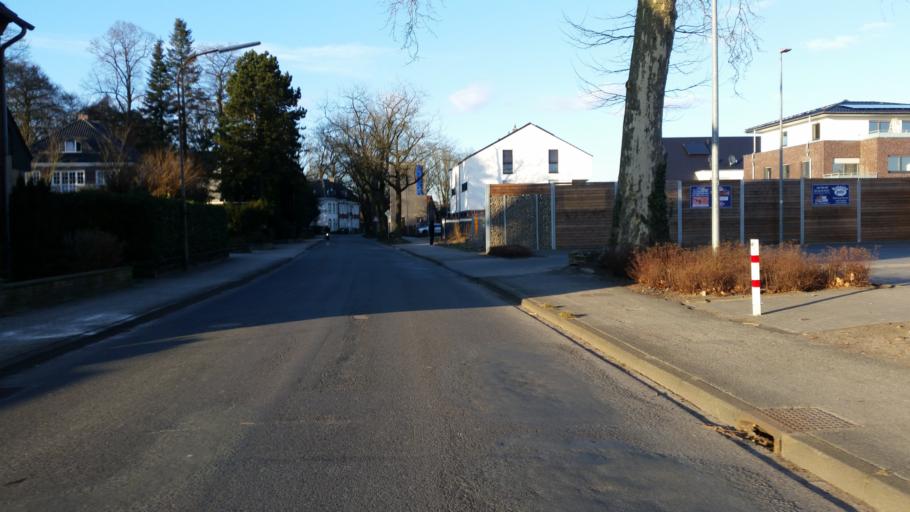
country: DE
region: North Rhine-Westphalia
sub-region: Regierungsbezirk Munster
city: Neuenkirchen
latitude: 52.2408
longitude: 7.3676
